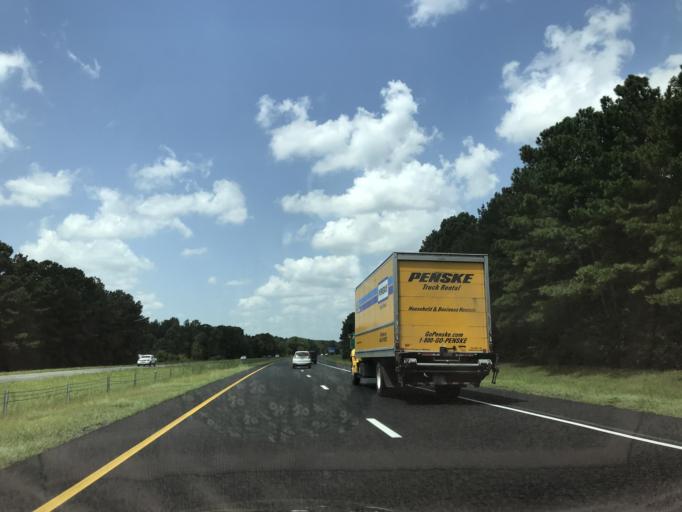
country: US
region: North Carolina
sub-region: Duplin County
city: Warsaw
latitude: 34.9748
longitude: -78.1244
